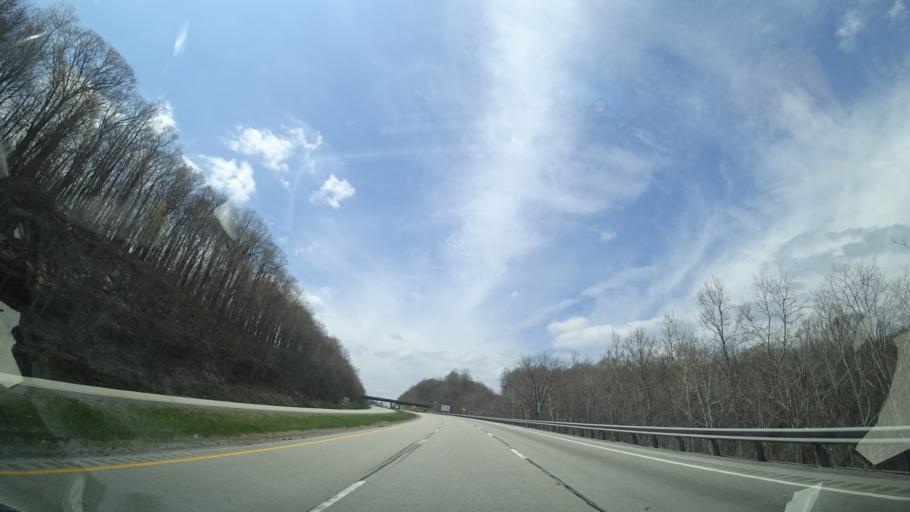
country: US
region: West Virginia
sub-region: Monongalia County
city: Cheat Lake
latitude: 39.6558
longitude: -79.7596
